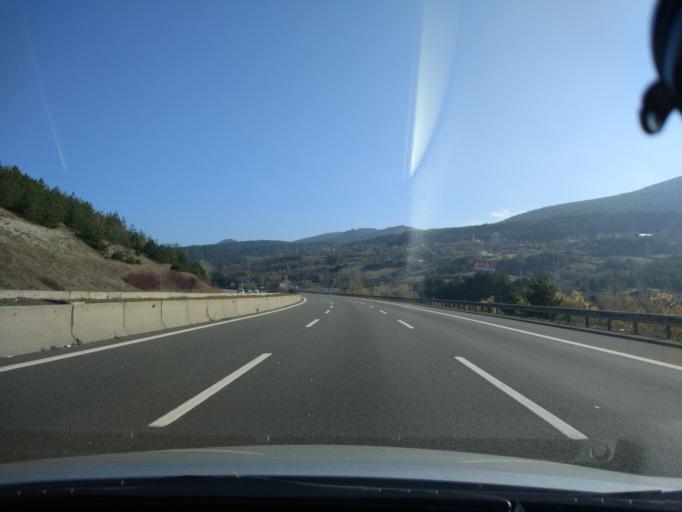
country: TR
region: Bolu
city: Bolu
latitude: 40.7349
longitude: 31.8030
